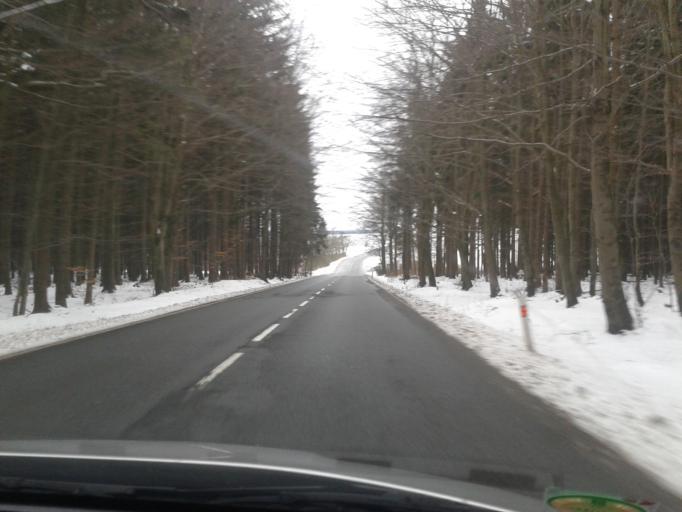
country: CZ
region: Olomoucky
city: Protivanov
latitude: 49.4719
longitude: 16.7826
